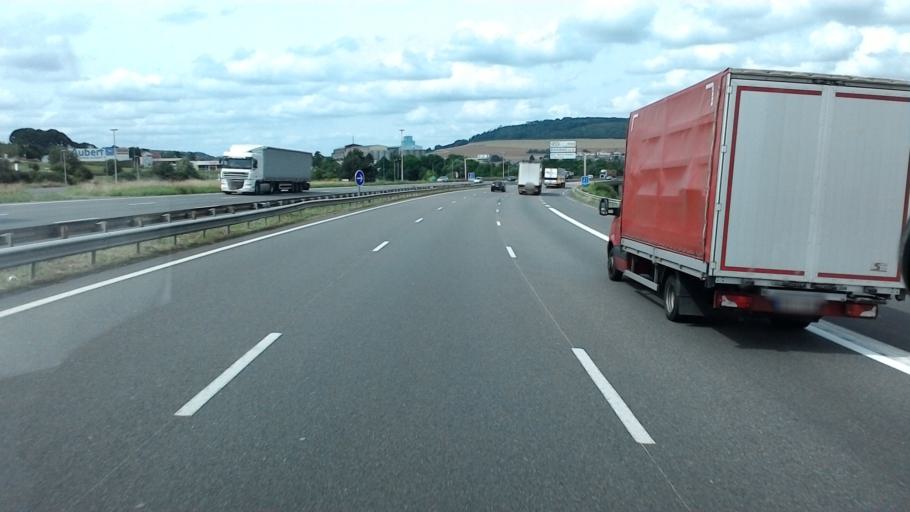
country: FR
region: Lorraine
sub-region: Departement de Meurthe-et-Moselle
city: Champigneulles
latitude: 48.7422
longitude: 6.1531
